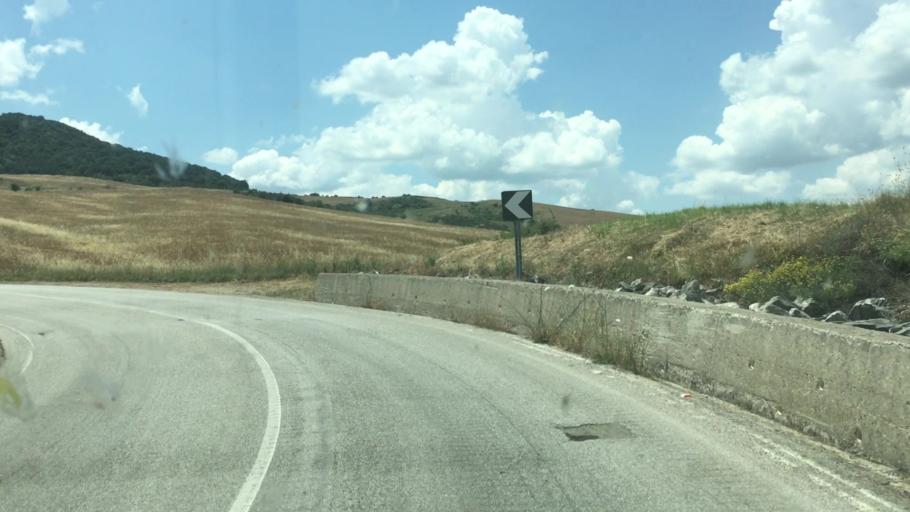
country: IT
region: Basilicate
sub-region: Provincia di Potenza
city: Tolve
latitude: 40.6924
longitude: 15.9872
